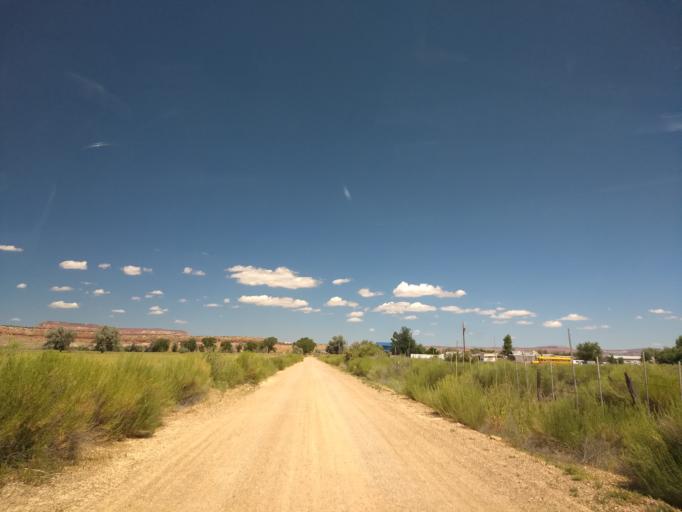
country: US
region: Arizona
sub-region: Coconino County
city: Fredonia
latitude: 36.9305
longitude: -112.5399
